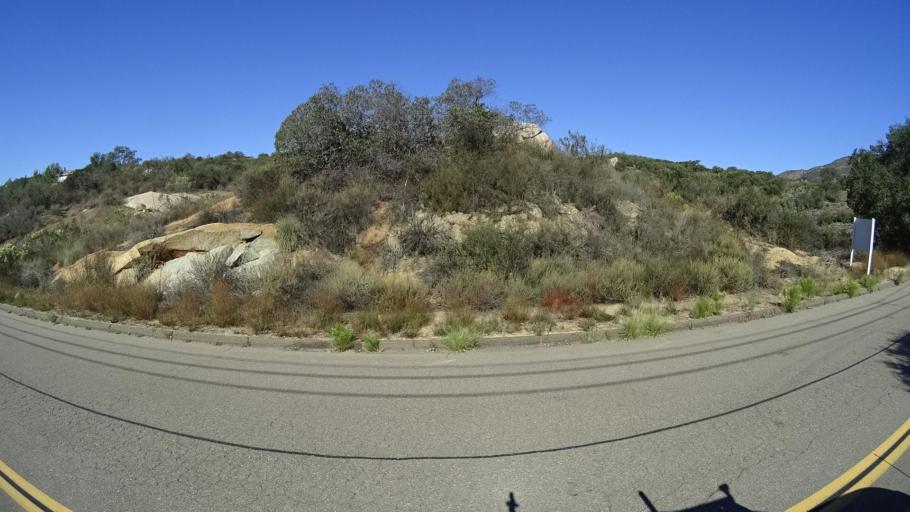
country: US
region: California
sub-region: San Diego County
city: Jamul
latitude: 32.7259
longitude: -116.8443
